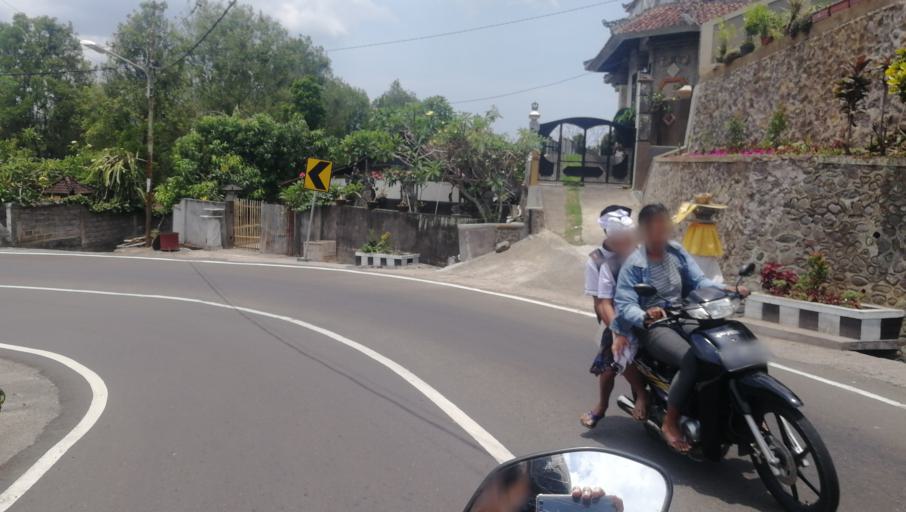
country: ID
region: Bali
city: Banjar Pedawa
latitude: -8.2630
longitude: 115.0340
